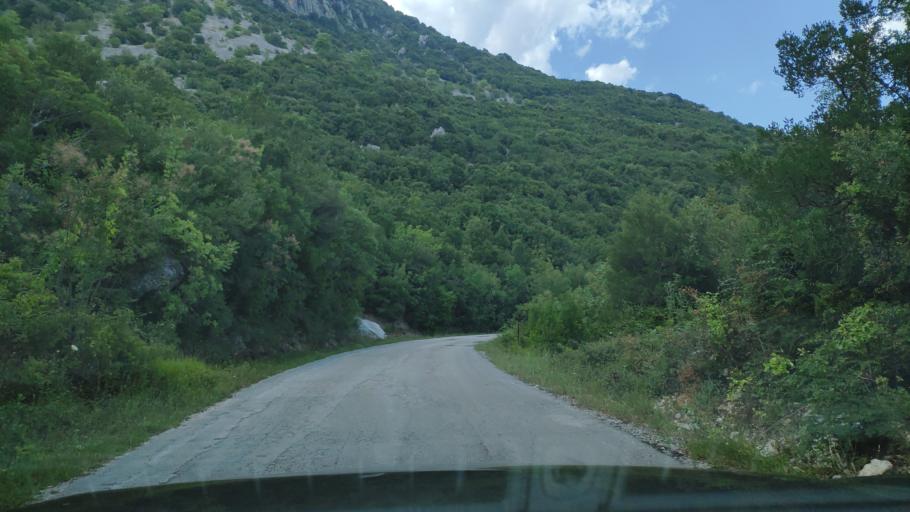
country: GR
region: Epirus
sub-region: Nomos Artas
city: Agios Dimitrios
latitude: 39.4464
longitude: 21.0167
